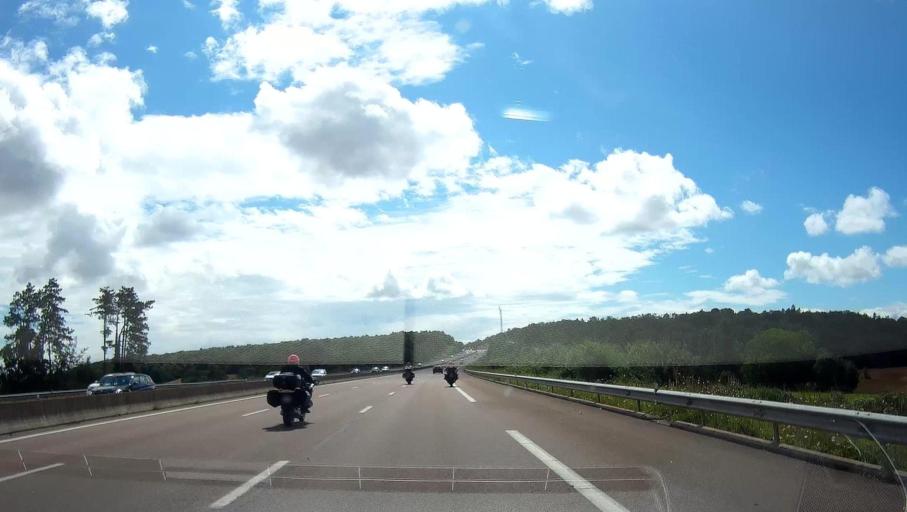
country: FR
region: Bourgogne
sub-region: Departement de la Cote-d'Or
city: Selongey
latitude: 47.5708
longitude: 5.2068
